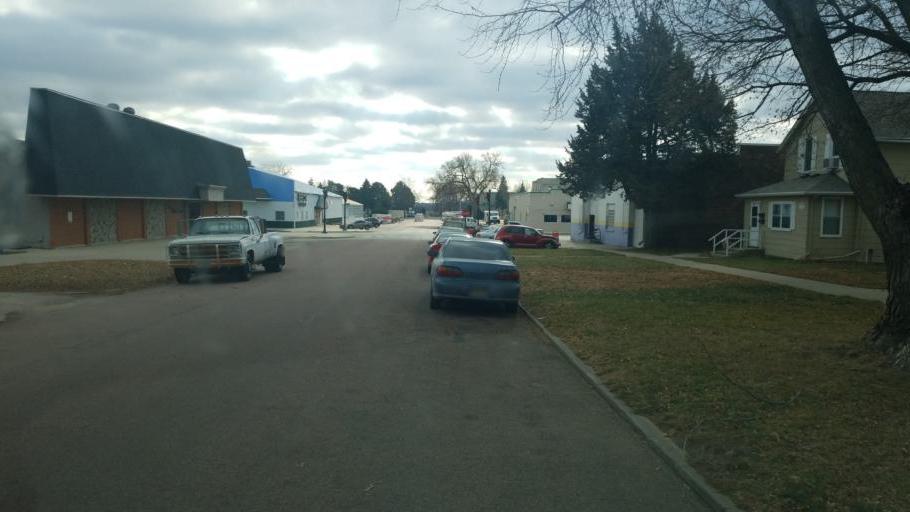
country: US
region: South Dakota
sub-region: Yankton County
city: Yankton
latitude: 42.8704
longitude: -97.3890
